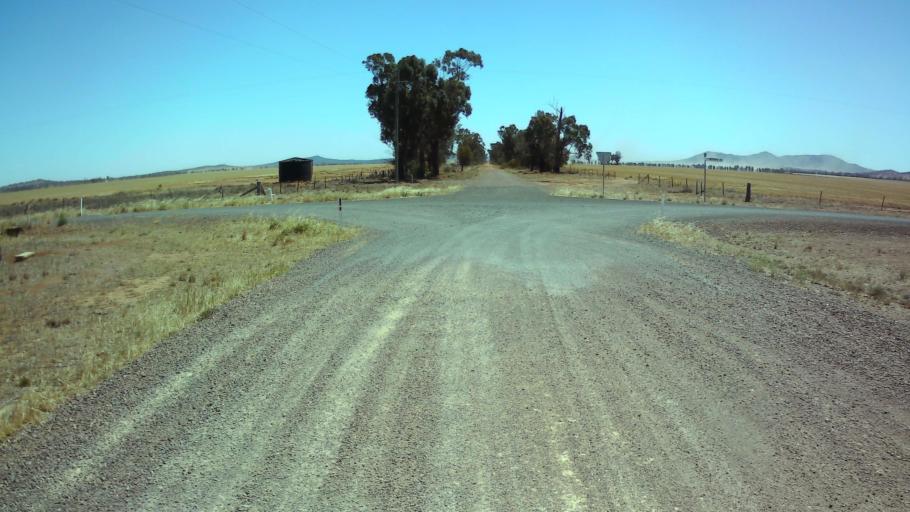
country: AU
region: New South Wales
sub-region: Forbes
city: Forbes
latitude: -33.6793
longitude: 147.7106
